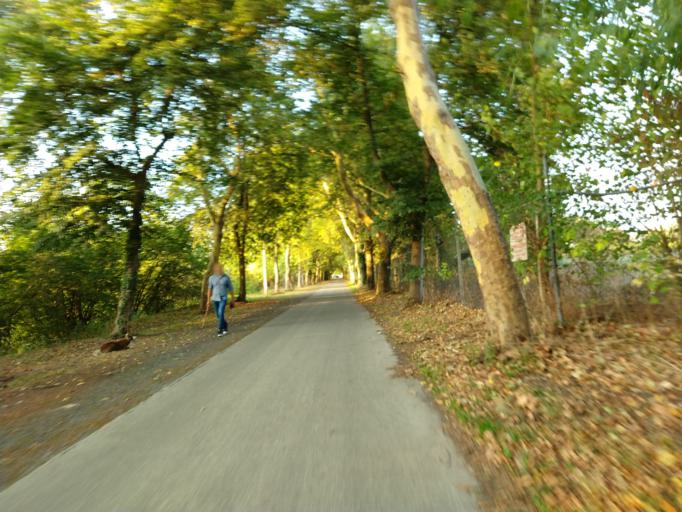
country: BE
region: Flanders
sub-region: Provincie Vlaams-Brabant
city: Hoegaarden
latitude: 50.7709
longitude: 4.8982
